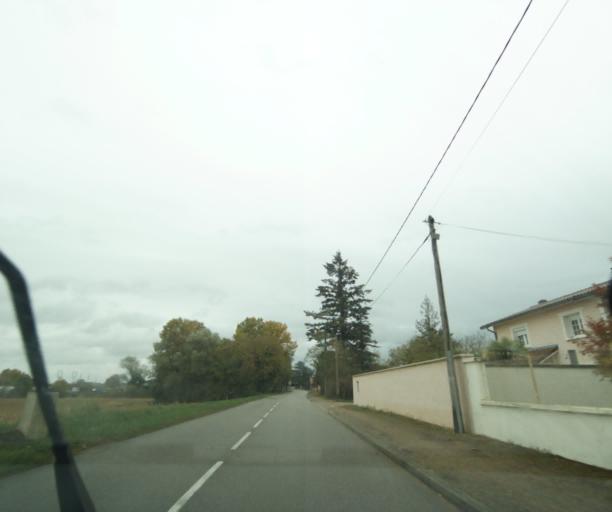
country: FR
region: Rhone-Alpes
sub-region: Departement de l'Ain
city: Saint-Jean-de-Niost
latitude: 45.8038
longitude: 5.2390
